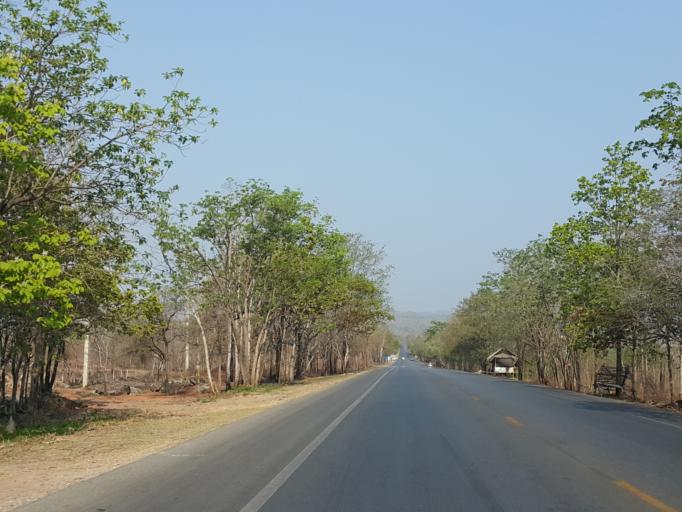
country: TH
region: Kanchanaburi
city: Sai Yok
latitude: 14.0951
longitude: 99.2576
